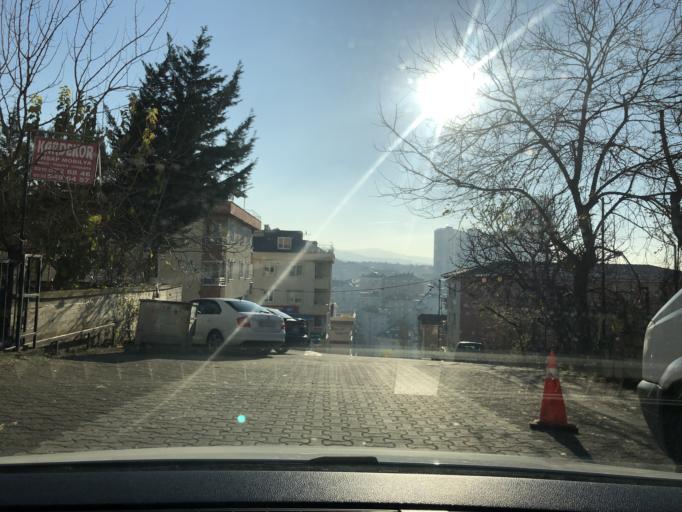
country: TR
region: Istanbul
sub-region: Atasehir
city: Atasehir
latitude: 40.9724
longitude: 29.1217
